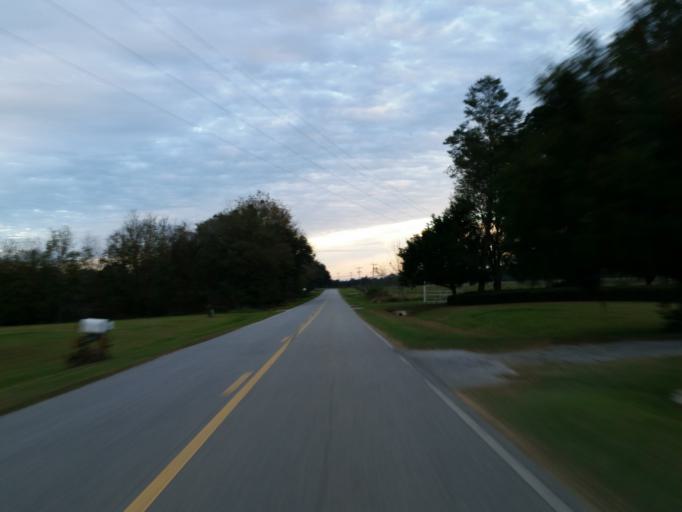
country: US
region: Florida
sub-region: Hamilton County
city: Jasper
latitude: 30.5229
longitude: -83.0841
